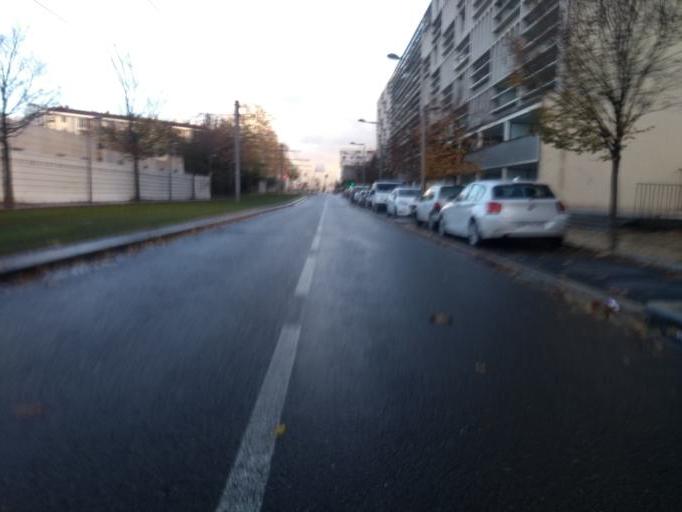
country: FR
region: Aquitaine
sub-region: Departement de la Gironde
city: Begles
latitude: 44.8171
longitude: -0.5529
